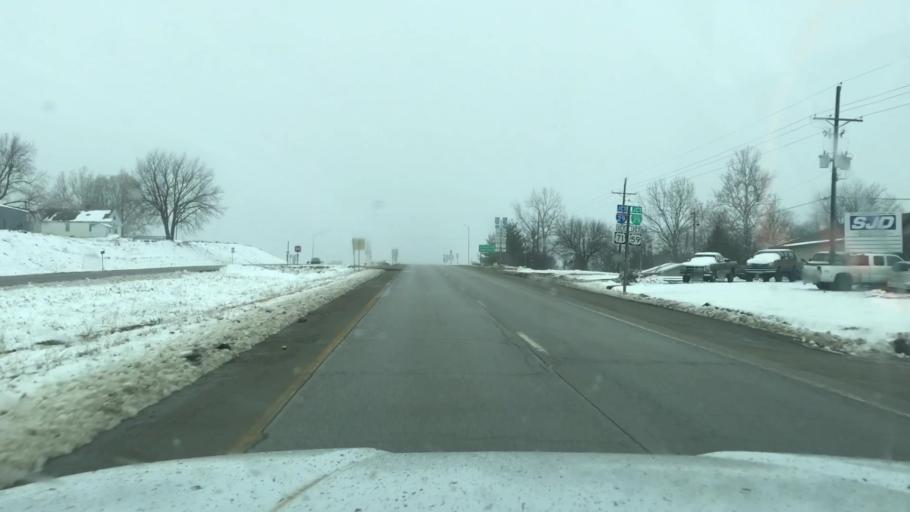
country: US
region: Missouri
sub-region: Andrew County
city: Country Club Village
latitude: 39.8619
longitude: -94.8096
